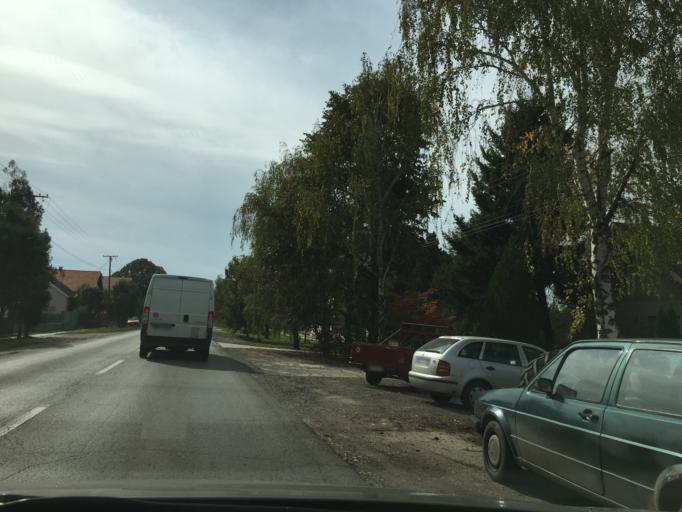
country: RS
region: Autonomna Pokrajina Vojvodina
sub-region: Juznobacki Okrug
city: Temerin
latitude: 45.3804
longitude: 19.8768
